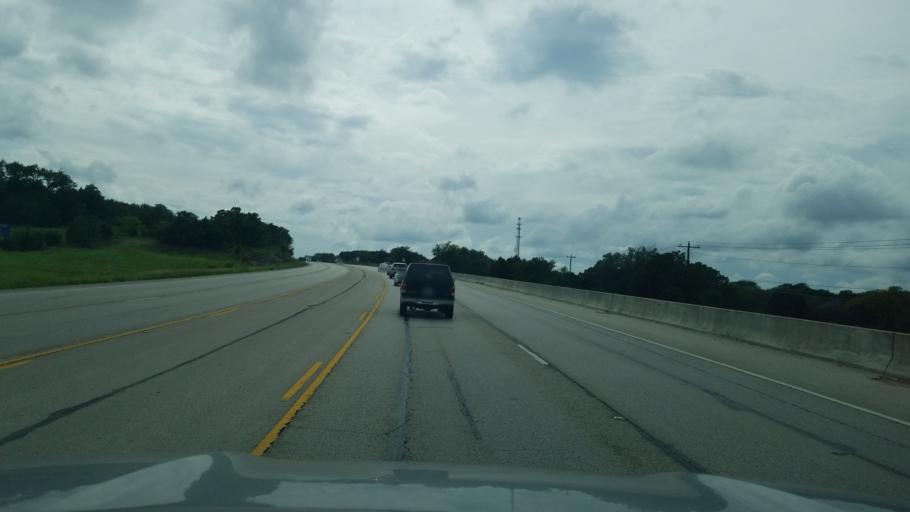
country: US
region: Texas
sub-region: Travis County
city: Bee Cave
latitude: 30.2174
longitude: -97.9626
